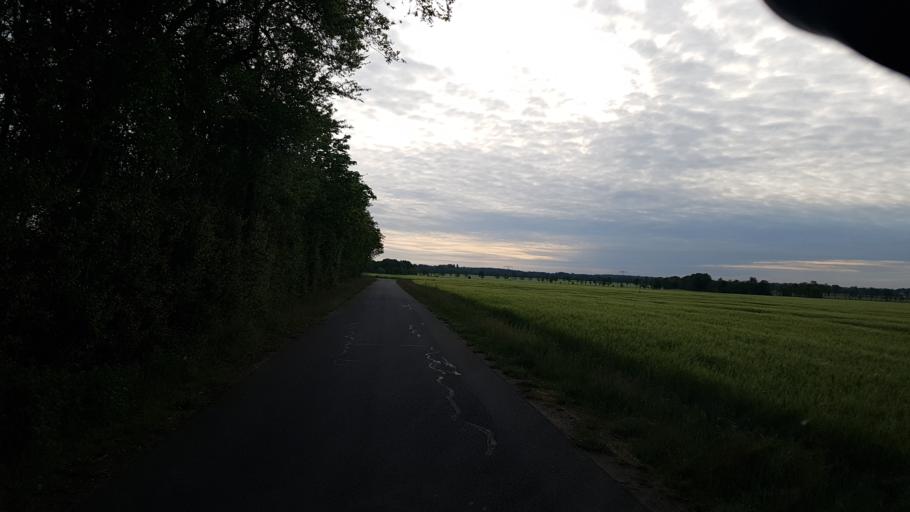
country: DE
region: Brandenburg
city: Luckau
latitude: 51.8113
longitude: 13.6378
